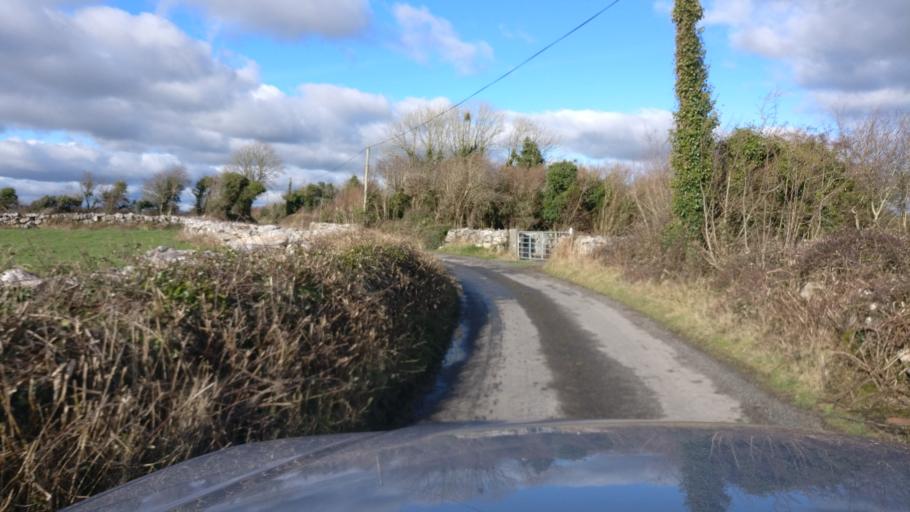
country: IE
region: Connaught
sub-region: County Galway
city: Athenry
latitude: 53.2293
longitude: -8.7995
